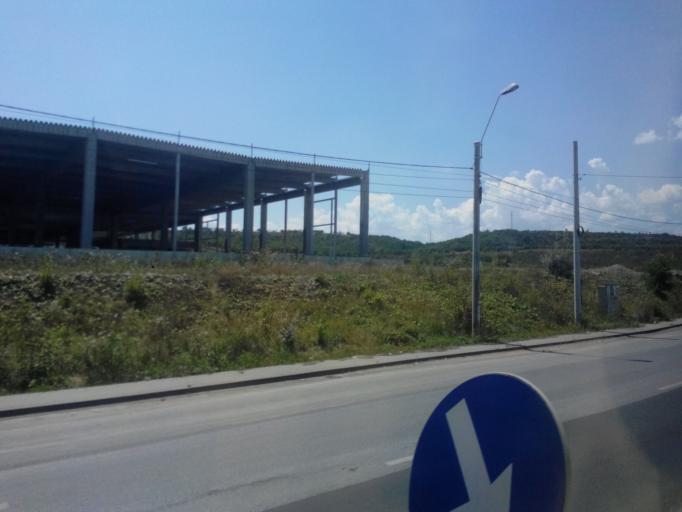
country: RO
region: Hunedoara
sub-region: Municipiul Deva
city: Cristur
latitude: 45.8582
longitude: 22.9424
